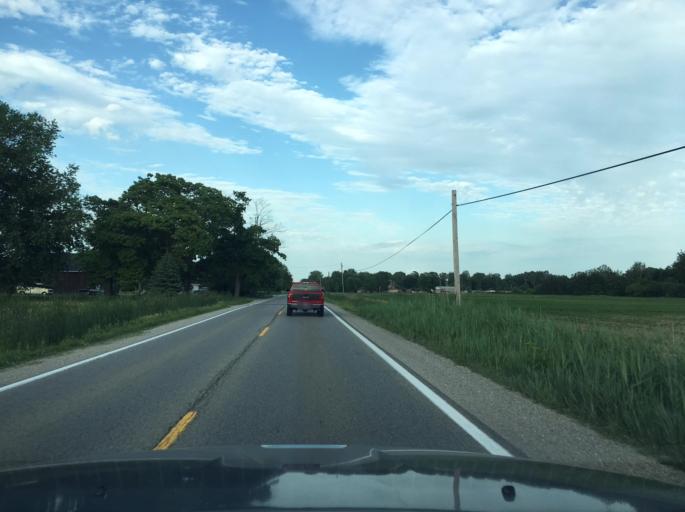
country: US
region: Michigan
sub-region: Macomb County
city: New Haven
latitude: 42.7171
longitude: -82.9124
